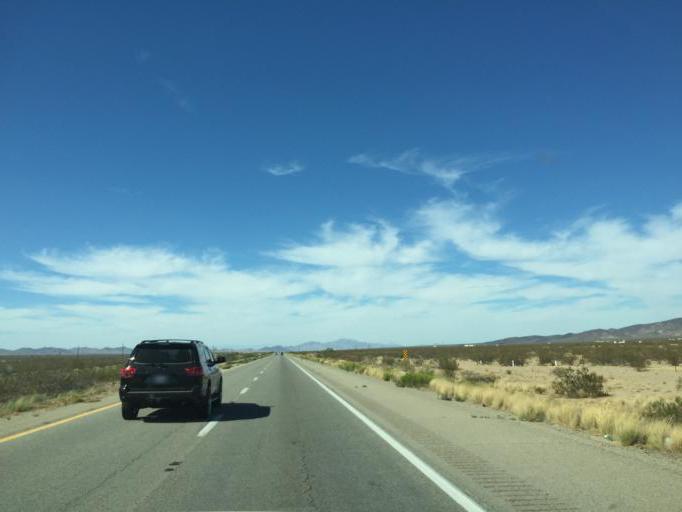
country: US
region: Arizona
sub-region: Mohave County
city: Dolan Springs
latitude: 35.5823
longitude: -114.3887
